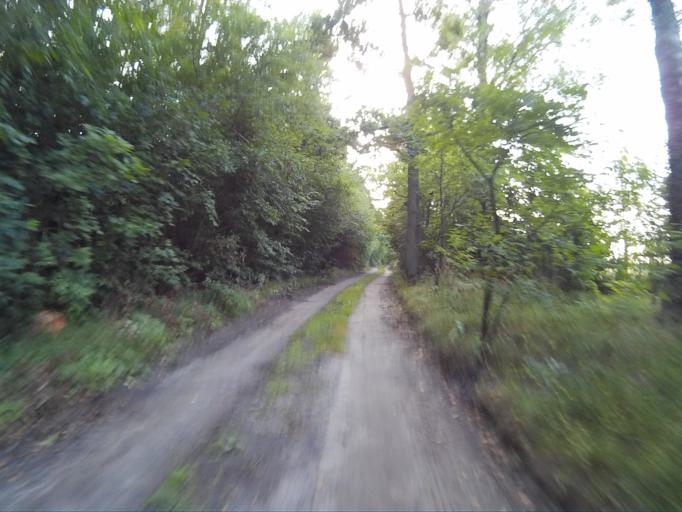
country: PL
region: Kujawsko-Pomorskie
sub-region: Powiat swiecki
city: Lniano
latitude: 53.5456
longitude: 18.1502
